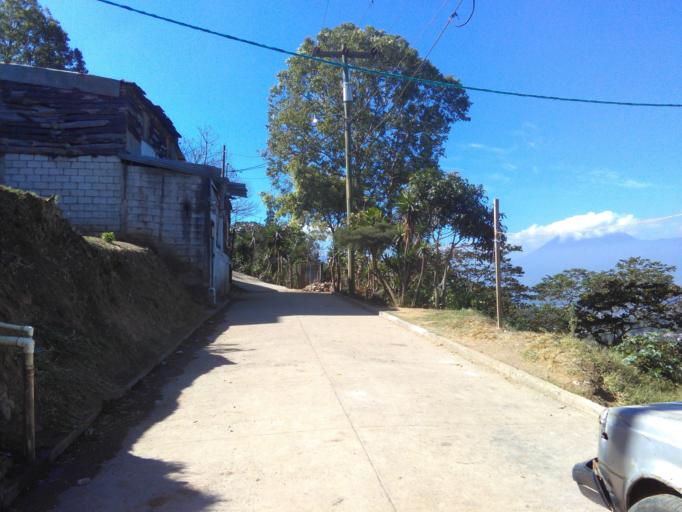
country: GT
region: Guatemala
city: Villa Canales
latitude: 14.5047
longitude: -90.5195
